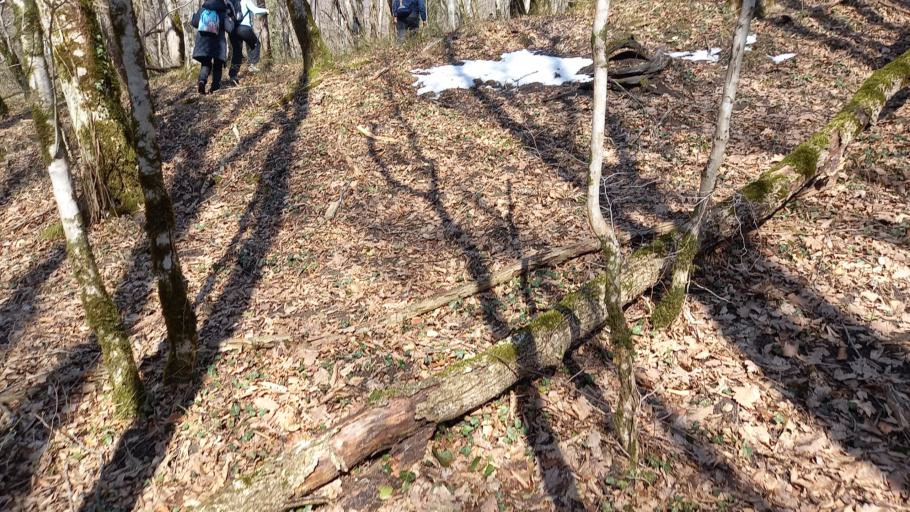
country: RU
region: Krasnodarskiy
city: Arkhipo-Osipovka
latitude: 44.3839
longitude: 38.6032
